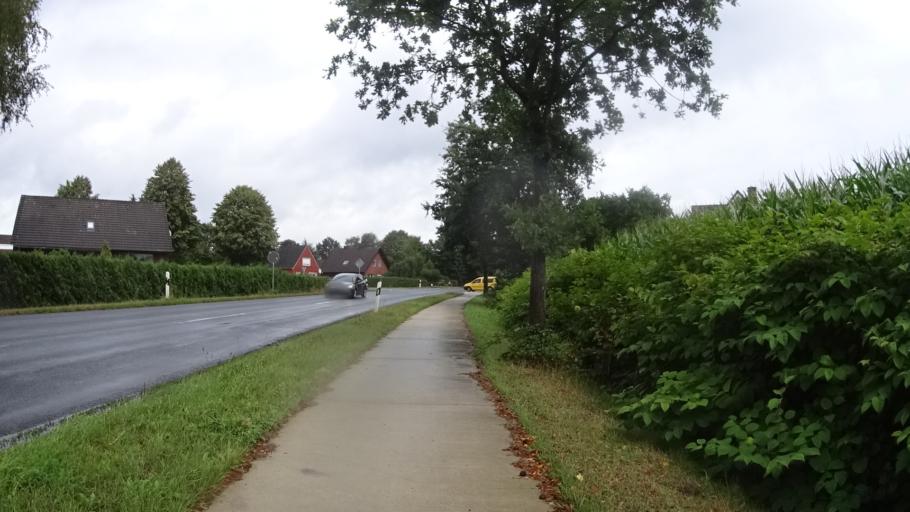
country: DE
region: Lower Saxony
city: Schwerinsdorf
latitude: 53.3428
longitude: 7.7003
